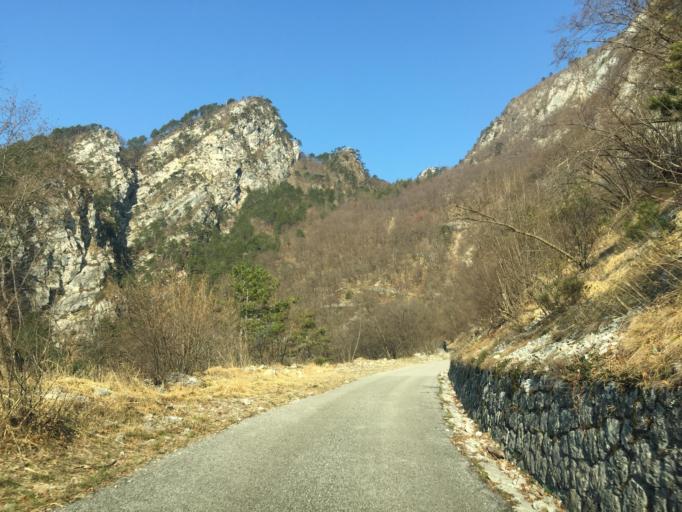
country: IT
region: Friuli Venezia Giulia
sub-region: Provincia di Udine
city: Amaro
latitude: 46.3878
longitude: 13.0810
